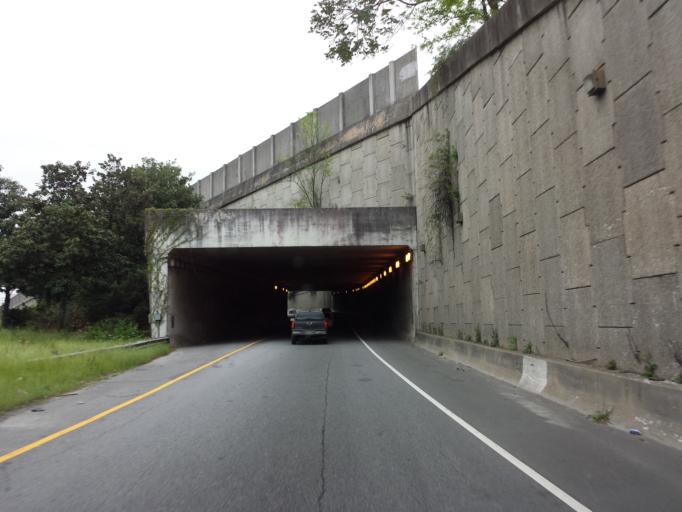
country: US
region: Georgia
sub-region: DeKalb County
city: Druid Hills
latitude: 33.8062
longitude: -84.3804
